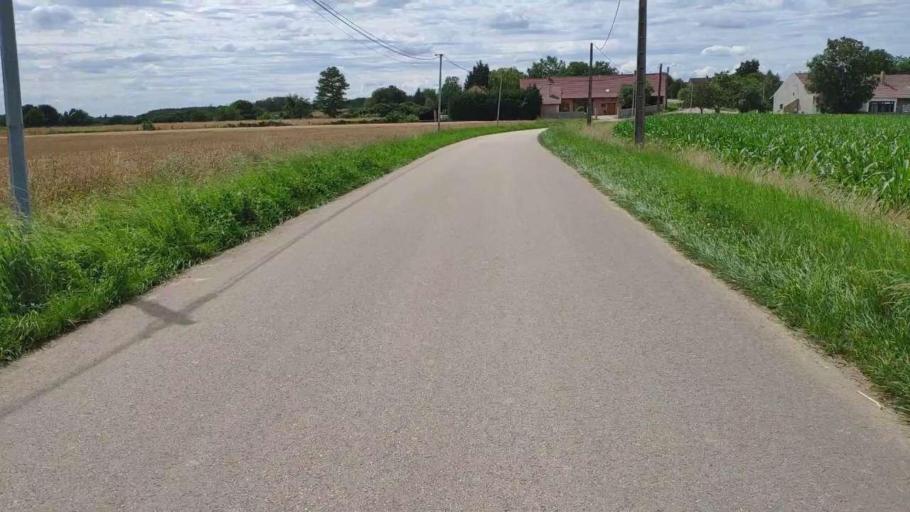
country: FR
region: Franche-Comte
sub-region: Departement du Jura
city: Chaussin
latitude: 46.8704
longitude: 5.4183
